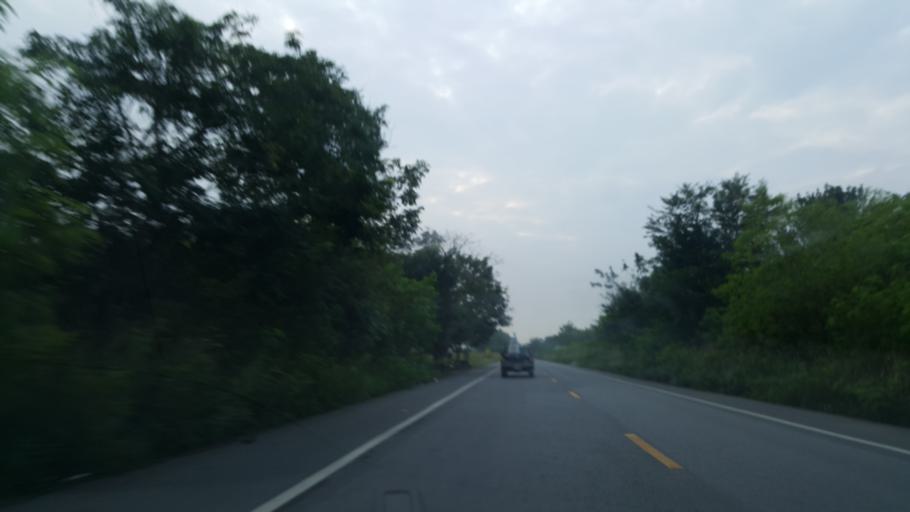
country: TH
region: Chon Buri
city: Sattahip
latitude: 12.7298
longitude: 100.9564
